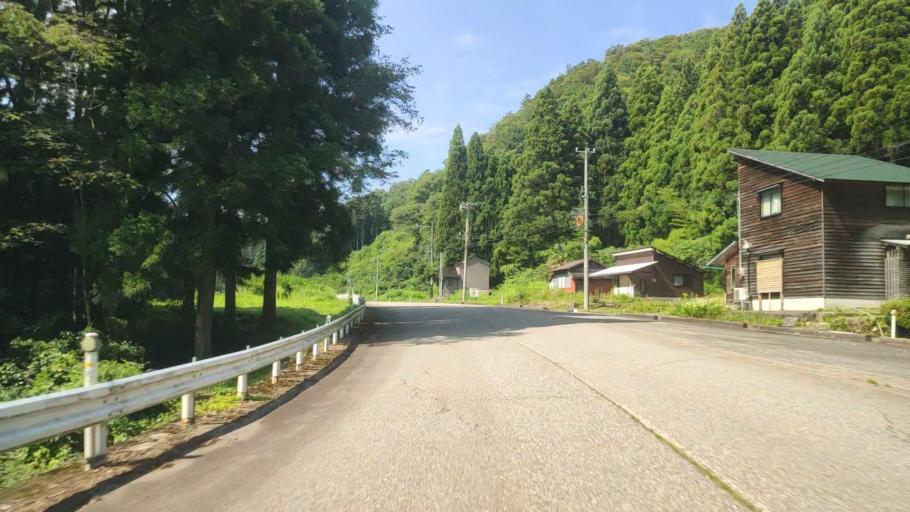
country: JP
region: Ishikawa
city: Komatsu
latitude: 36.3133
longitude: 136.5298
